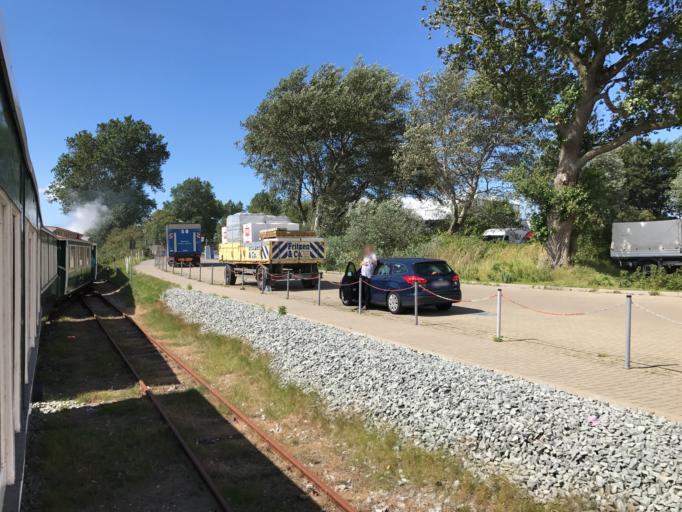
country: DE
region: Lower Saxony
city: Borkum
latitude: 53.5639
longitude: 6.7553
